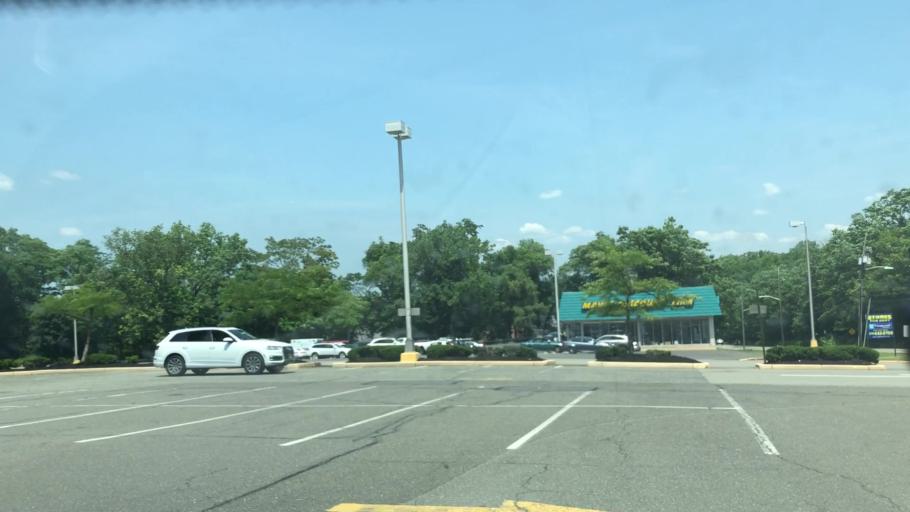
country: US
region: New Jersey
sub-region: Essex County
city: West Orange
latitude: 40.8058
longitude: -74.2471
